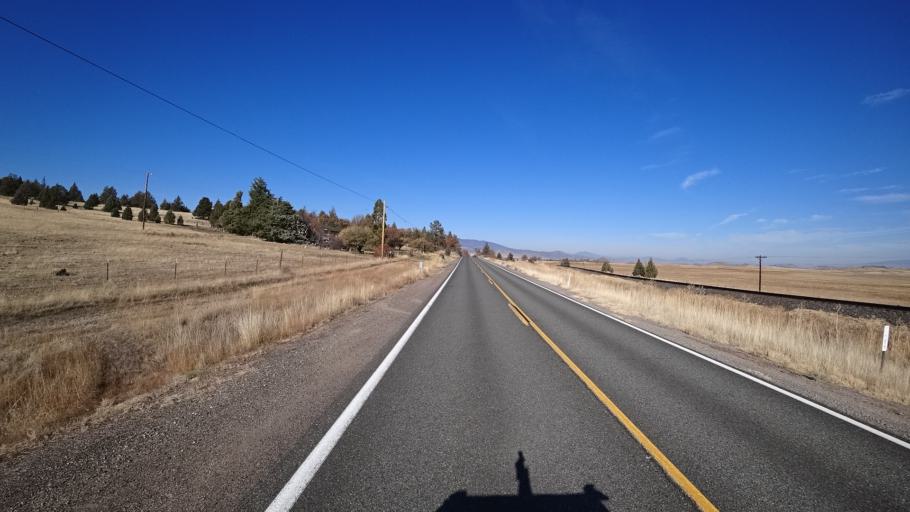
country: US
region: California
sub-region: Siskiyou County
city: Weed
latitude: 41.4936
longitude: -122.5096
